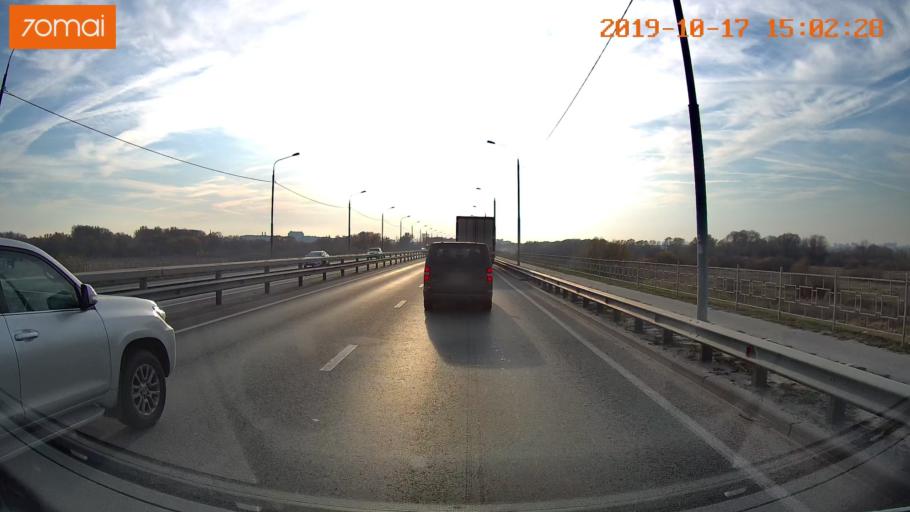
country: RU
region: Rjazan
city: Ryazan'
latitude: 54.6453
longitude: 39.7419
